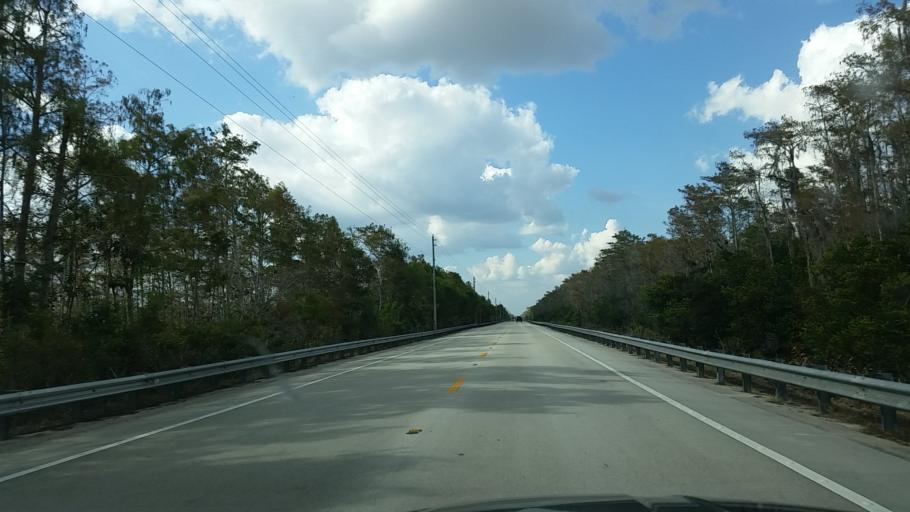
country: US
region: Florida
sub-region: Miami-Dade County
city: Kendall West
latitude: 25.7847
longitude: -80.8519
